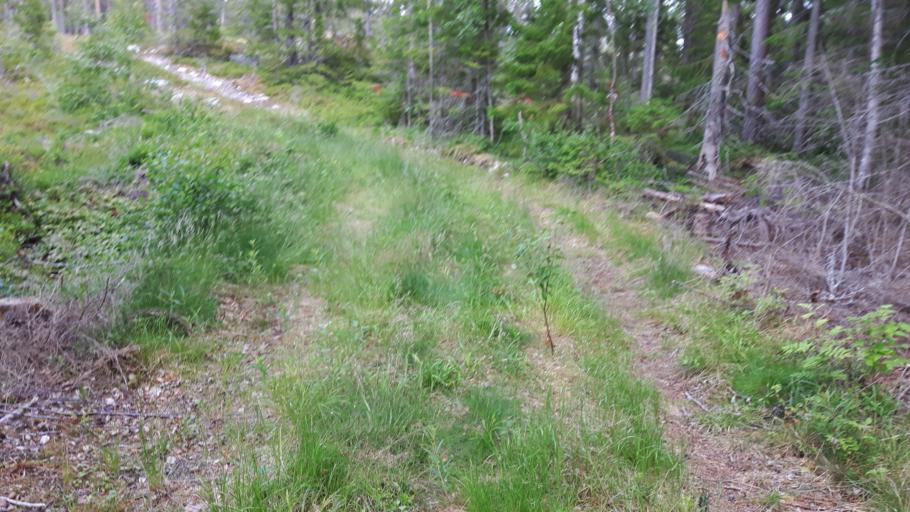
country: SE
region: Vaesternorrland
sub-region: Haernoesands Kommun
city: Haernoesand
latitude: 62.6809
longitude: 18.0449
